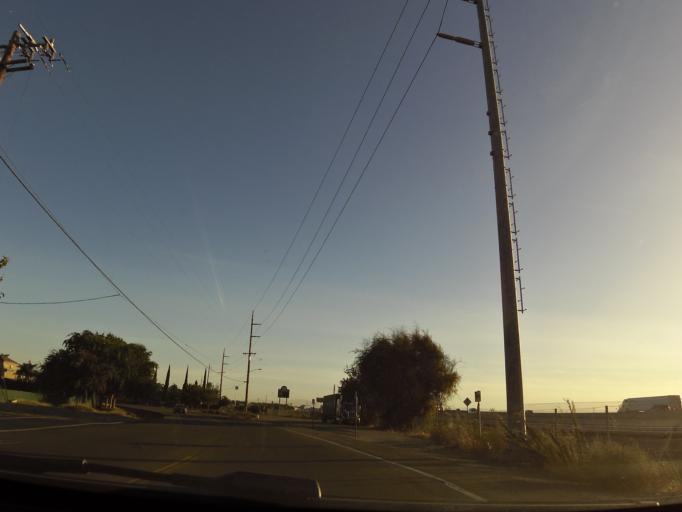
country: US
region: California
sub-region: San Joaquin County
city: Lathrop
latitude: 37.8301
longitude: -121.2881
